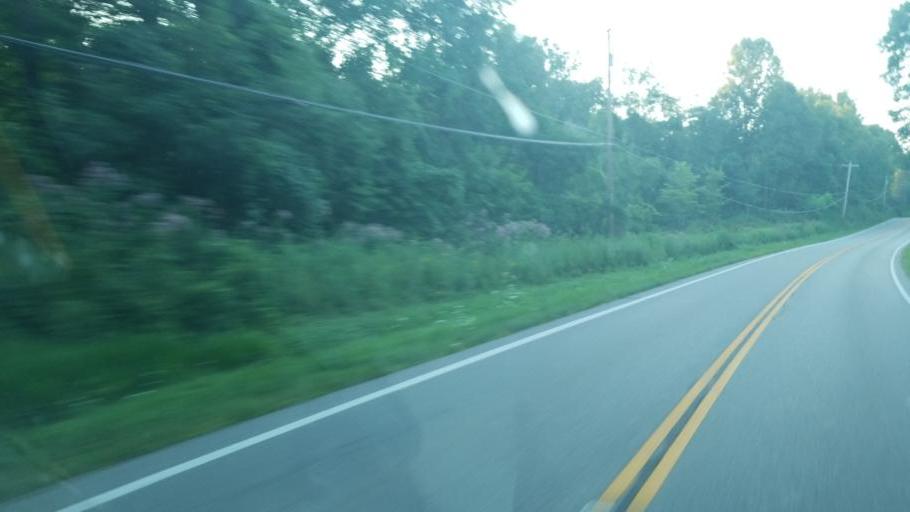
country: US
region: Ohio
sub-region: Trumbull County
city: Newton Falls
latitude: 41.2089
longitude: -80.9786
